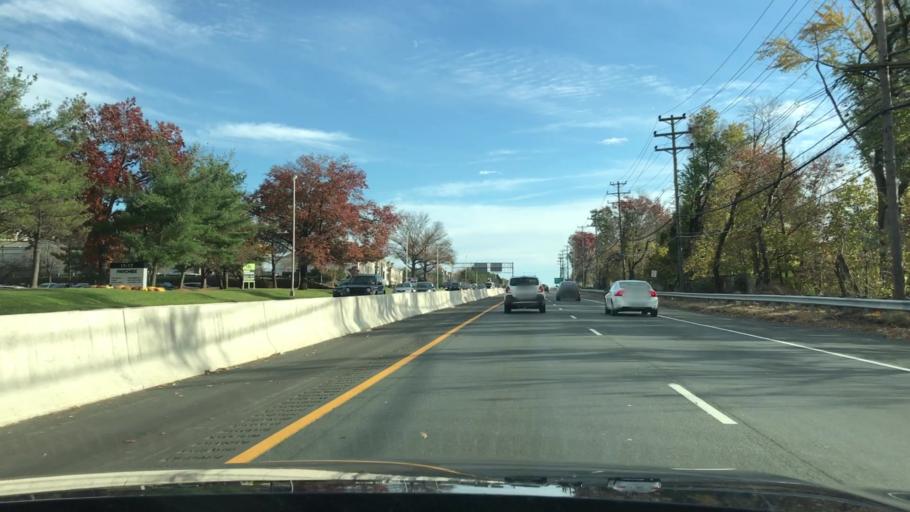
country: US
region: New Jersey
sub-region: Bergen County
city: Fair Lawn
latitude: 40.9444
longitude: -74.1314
